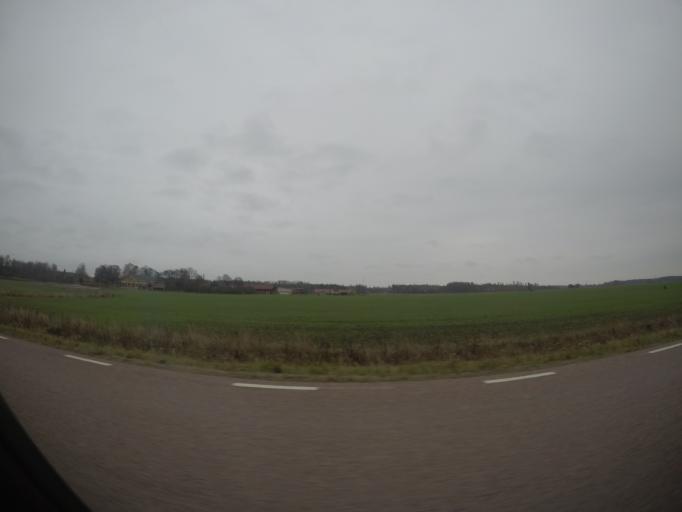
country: SE
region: Vaestmanland
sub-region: Kopings Kommun
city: Koping
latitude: 59.5667
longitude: 16.0932
